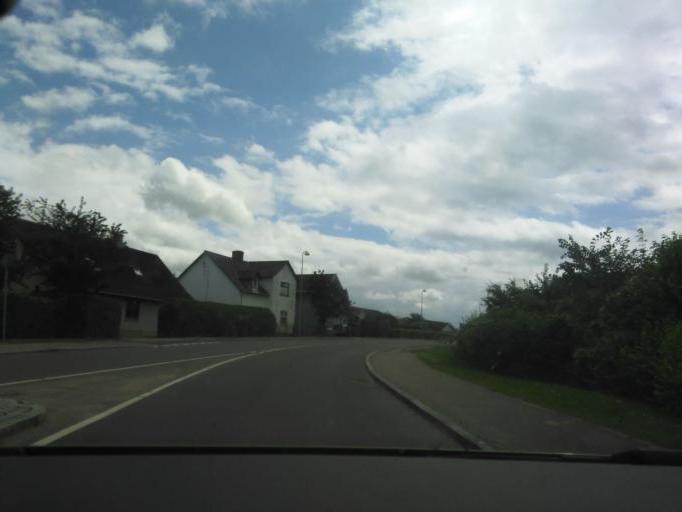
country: DK
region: Zealand
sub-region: Kalundborg Kommune
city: Gorlev
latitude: 55.5458
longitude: 11.2227
